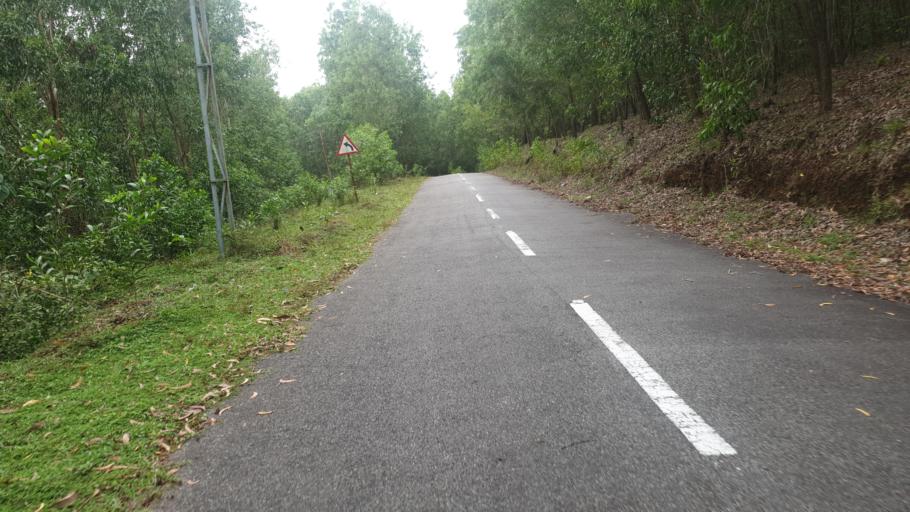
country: IN
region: Kerala
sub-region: Thiruvananthapuram
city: Nedumangad
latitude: 8.6311
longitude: 77.1222
